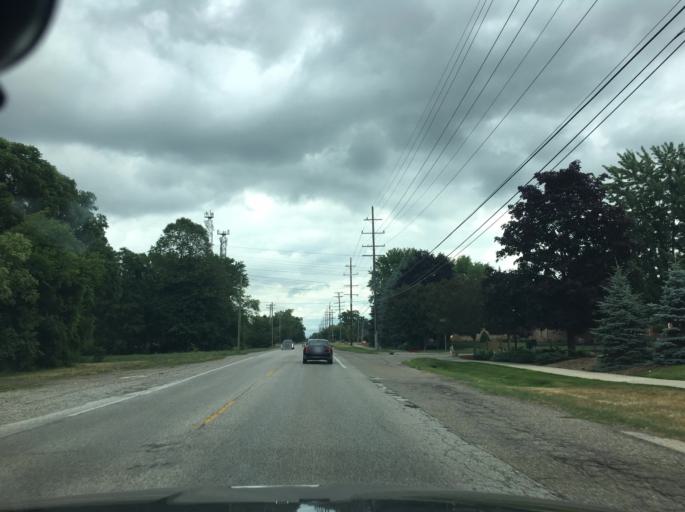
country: US
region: Michigan
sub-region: Macomb County
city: Shelby
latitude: 42.6554
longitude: -83.0058
